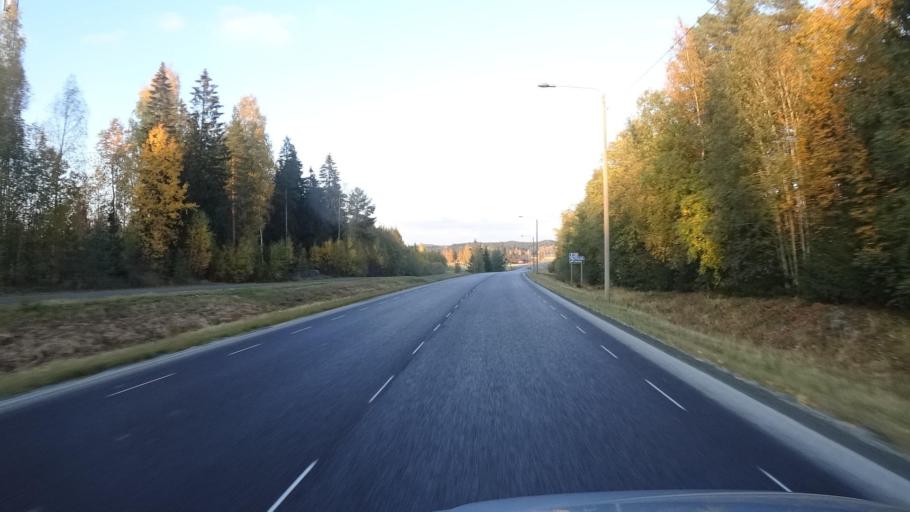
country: FI
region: Haeme
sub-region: Forssa
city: Jokioinen
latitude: 60.8177
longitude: 23.5459
